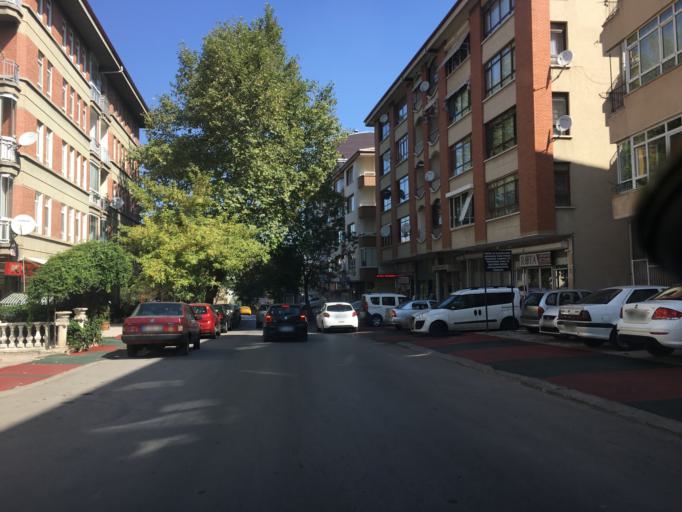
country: TR
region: Ankara
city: Ankara
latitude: 39.8983
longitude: 32.8505
